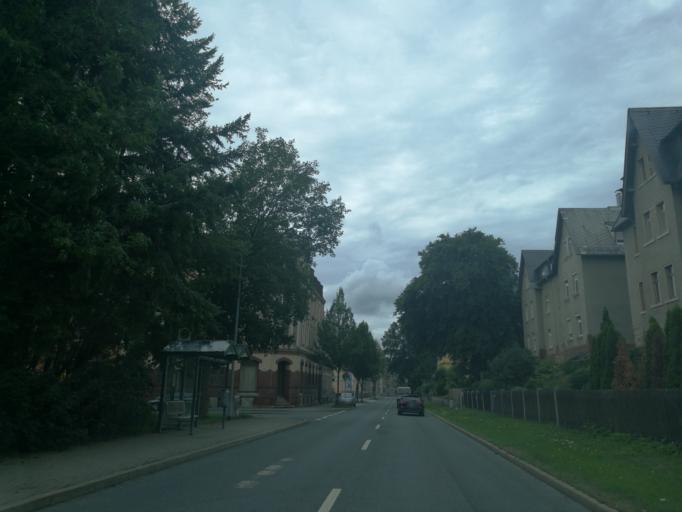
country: DE
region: Saxony
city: Adorf
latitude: 50.3189
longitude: 12.2670
